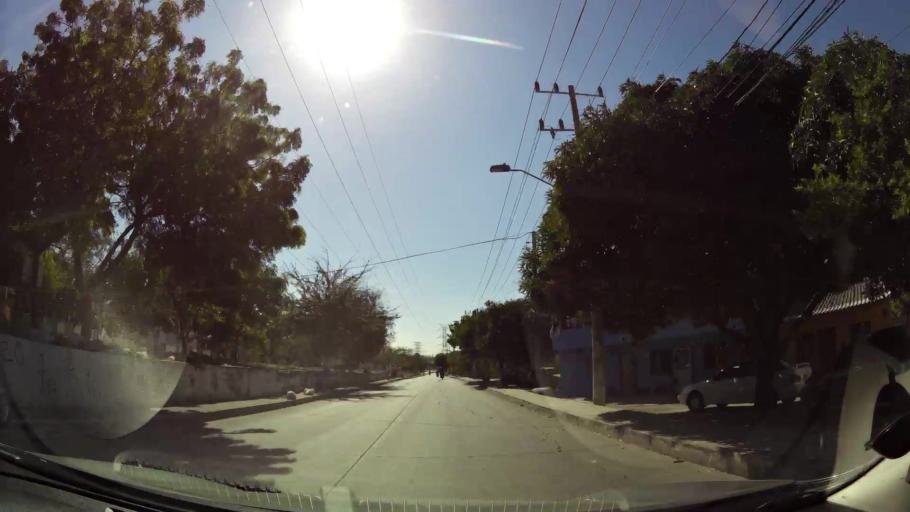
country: CO
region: Atlantico
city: Soledad
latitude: 10.9304
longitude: -74.7891
